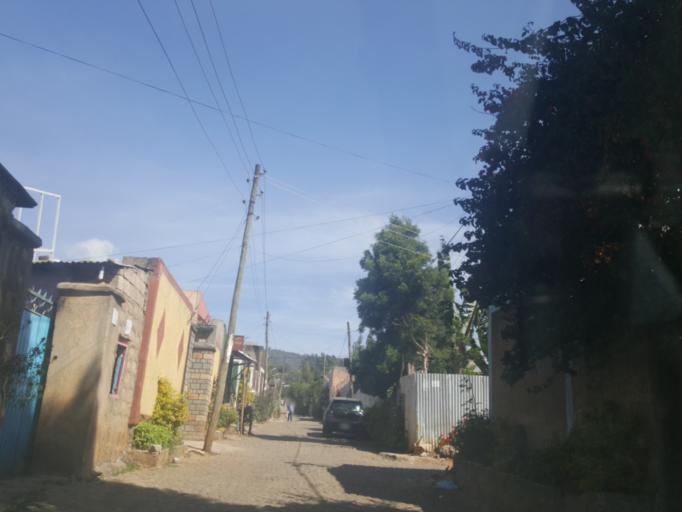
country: ET
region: Adis Abeba
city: Addis Ababa
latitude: 9.0645
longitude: 38.7254
